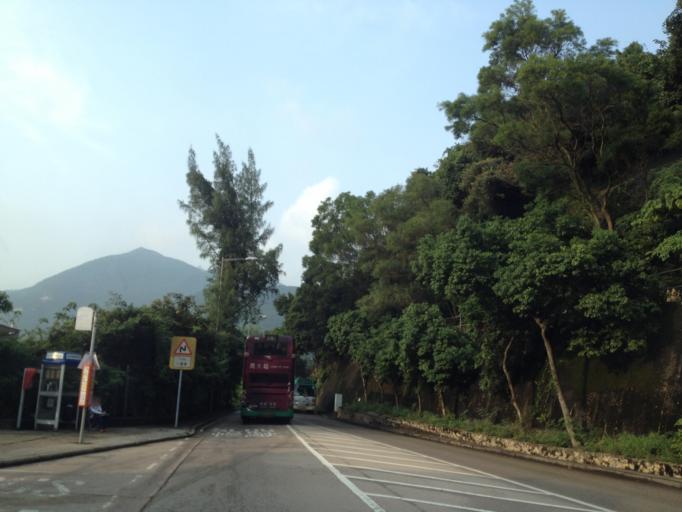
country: HK
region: Wanchai
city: Wan Chai
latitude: 22.2401
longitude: 114.2214
